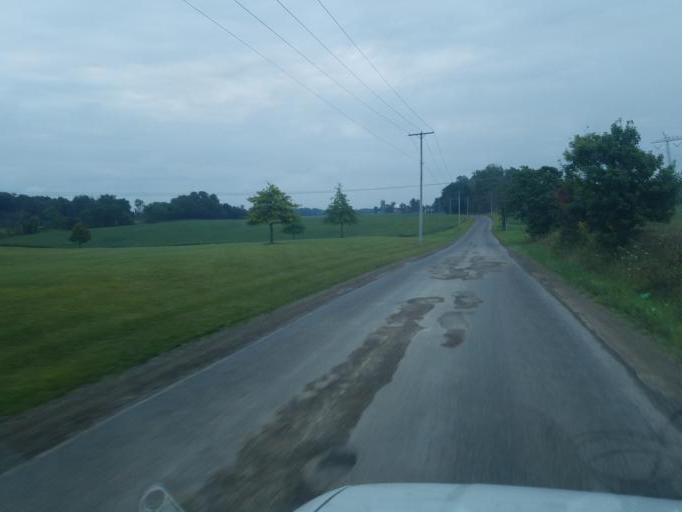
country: US
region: Ohio
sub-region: Richland County
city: Lexington
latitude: 40.5866
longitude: -82.6579
